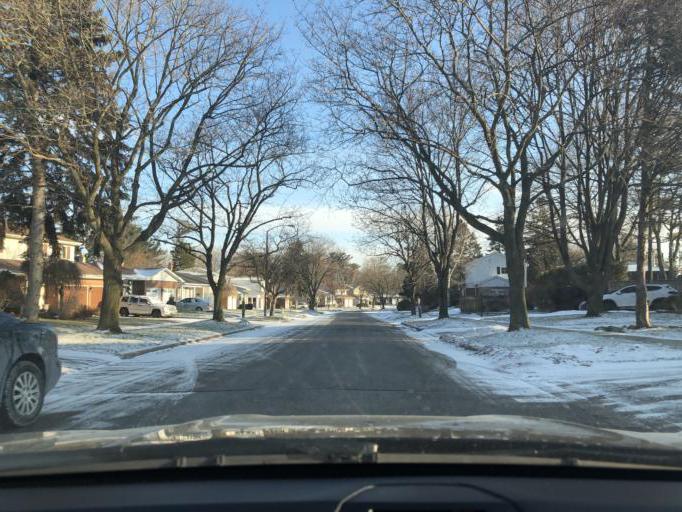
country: CA
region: Ontario
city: Scarborough
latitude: 43.7753
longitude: -79.1496
